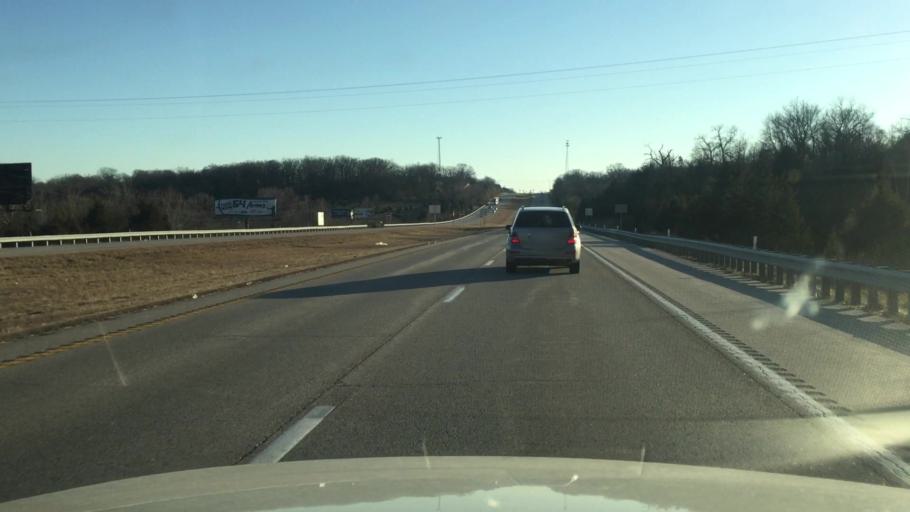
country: US
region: Missouri
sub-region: Cole County
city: Wardsville
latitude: 38.4923
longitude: -92.2698
